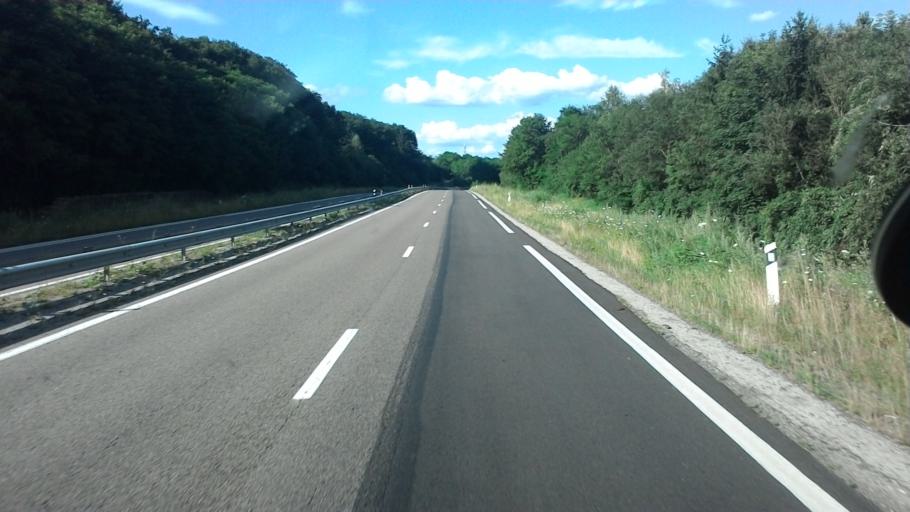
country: FR
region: Franche-Comte
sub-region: Departement de la Haute-Saone
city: Luxeuil-les-Bains
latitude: 47.7422
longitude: 6.3228
